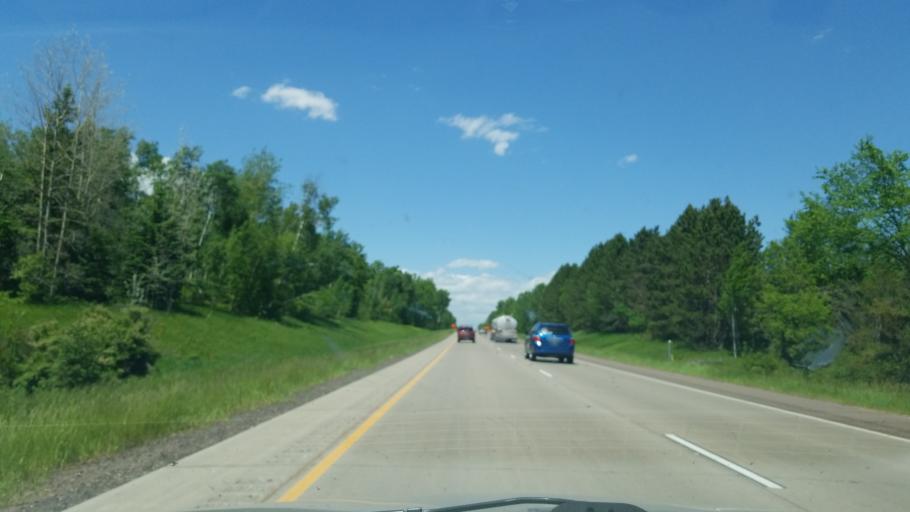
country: US
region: Minnesota
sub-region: Pine County
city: Sandstone
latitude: 46.2375
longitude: -92.8253
